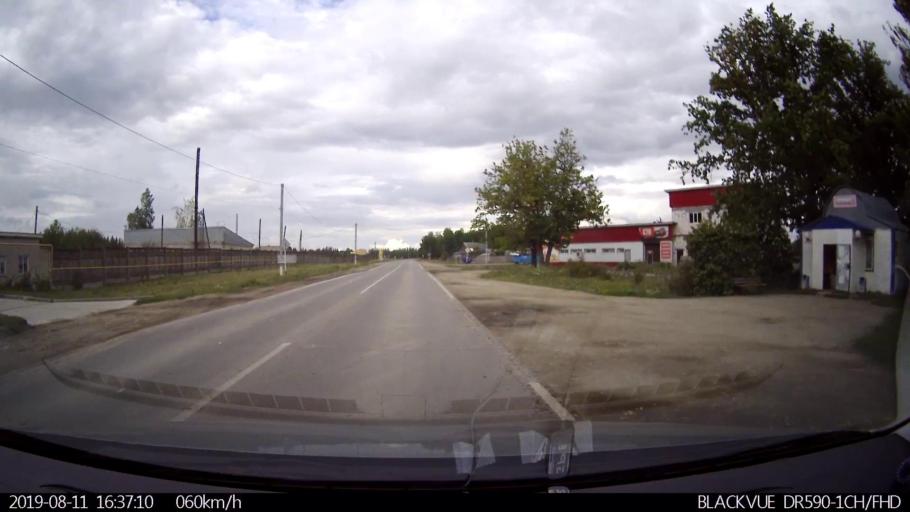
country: RU
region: Ulyanovsk
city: Mayna
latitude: 54.1250
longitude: 47.6126
